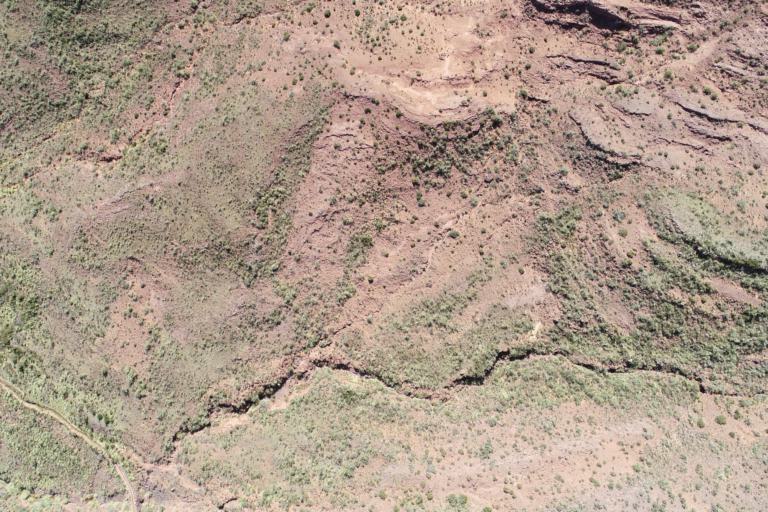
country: BO
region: La Paz
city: Tiahuanaco
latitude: -16.6055
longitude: -68.7562
